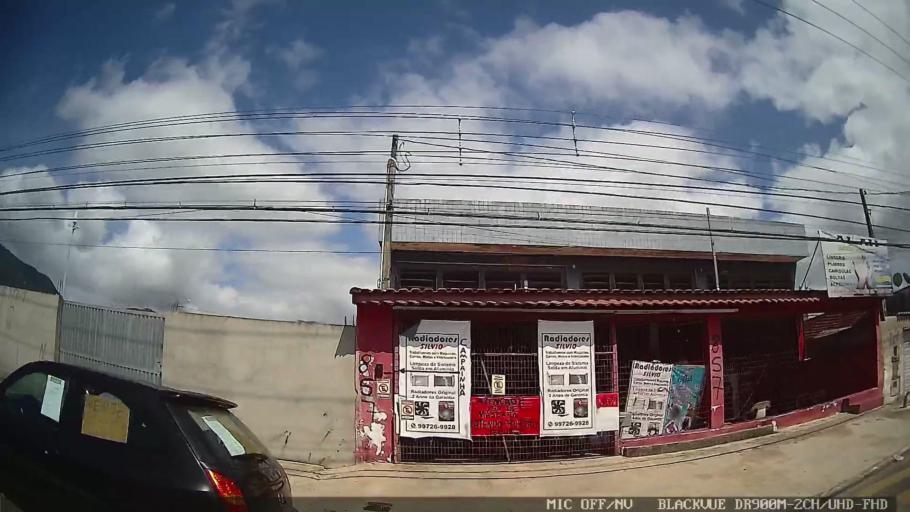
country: BR
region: Sao Paulo
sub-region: Peruibe
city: Peruibe
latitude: -24.3116
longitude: -47.0109
